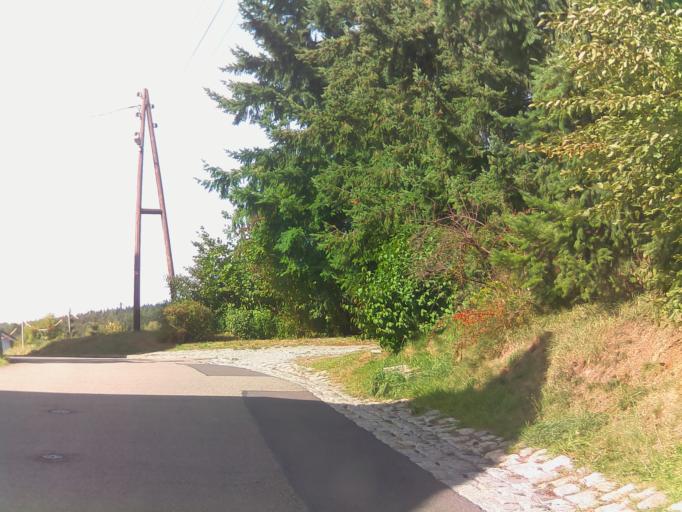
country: DE
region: Thuringia
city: Christes
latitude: 50.6609
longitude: 10.4784
